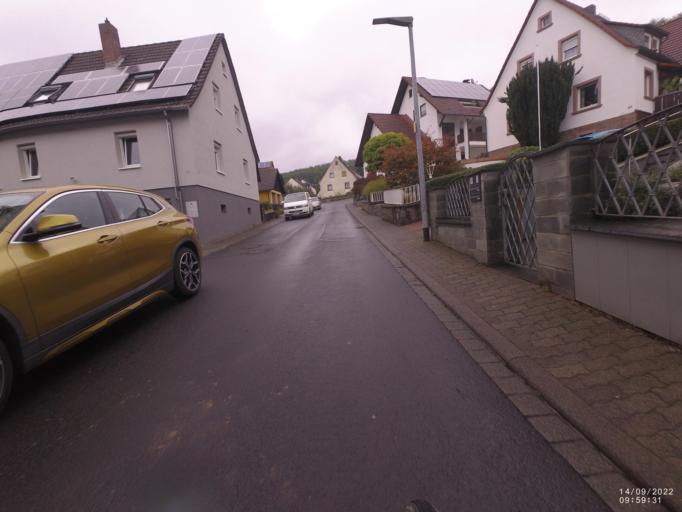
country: DE
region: Bavaria
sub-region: Regierungsbezirk Unterfranken
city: Glattbach
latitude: 50.0081
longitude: 9.1515
